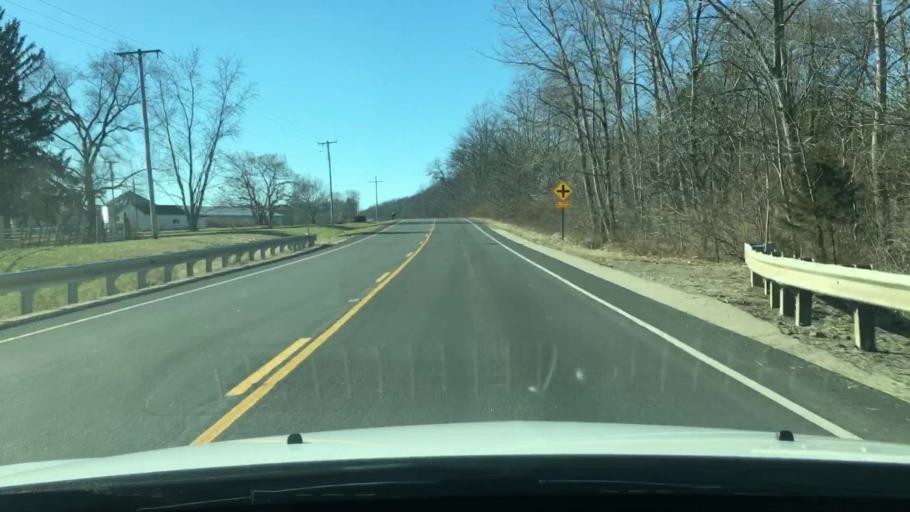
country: US
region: Illinois
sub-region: Mason County
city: Havana
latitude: 40.4182
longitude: -90.0090
